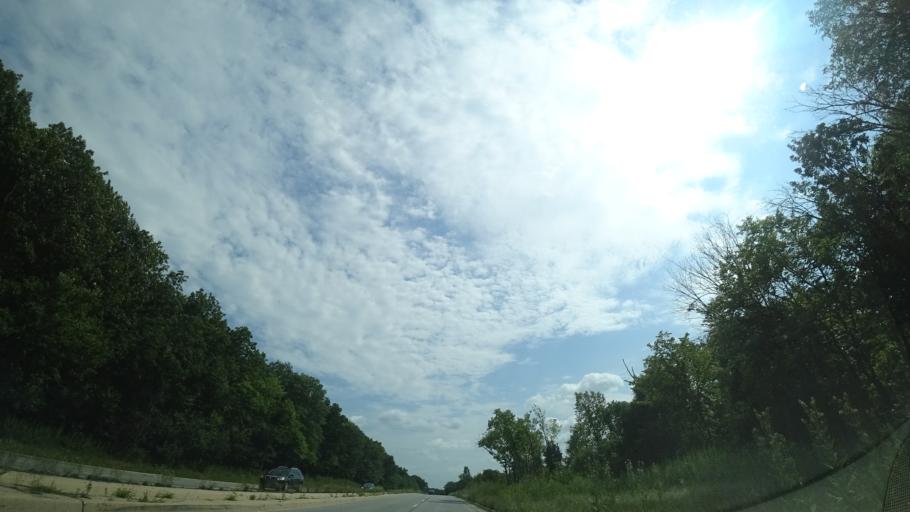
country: US
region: Illinois
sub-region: Cook County
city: Palos Heights
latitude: 41.6388
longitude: -87.7955
